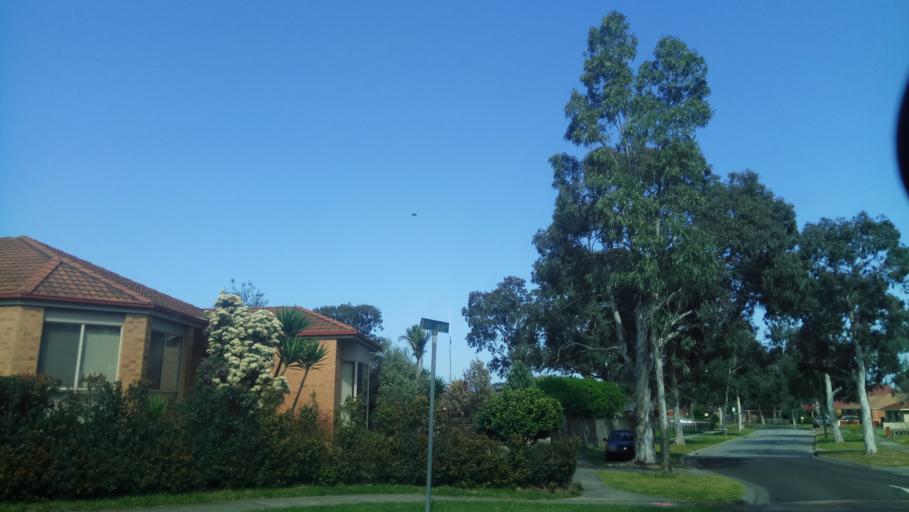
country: AU
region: Victoria
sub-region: Casey
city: Lynbrook
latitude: -38.0508
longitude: 145.2531
